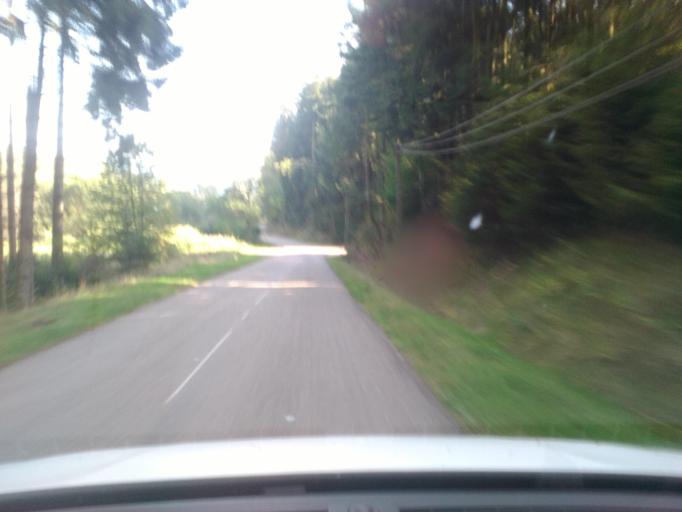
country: FR
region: Lorraine
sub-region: Departement des Vosges
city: Ban-de-Laveline
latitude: 48.3198
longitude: 7.0739
